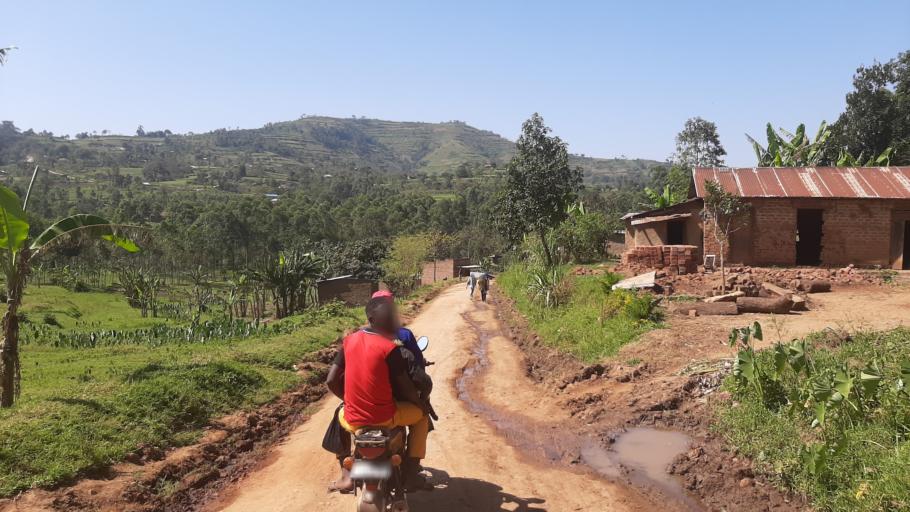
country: UG
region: Eastern Region
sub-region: Manafwa District
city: Manafwa
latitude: 0.9109
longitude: 34.3287
